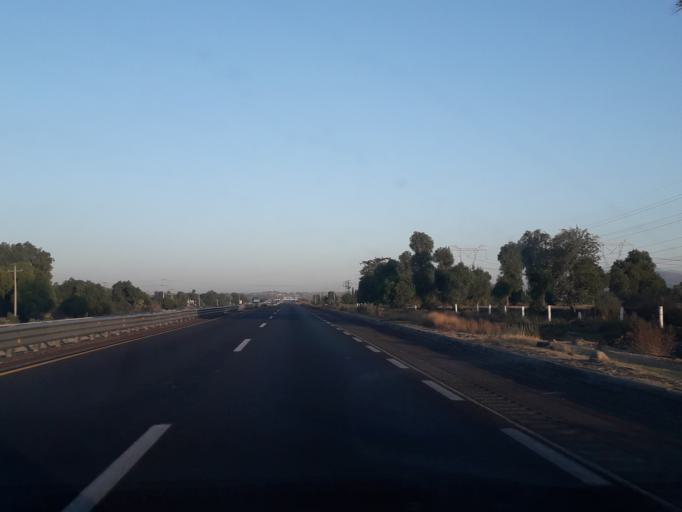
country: MX
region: Puebla
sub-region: Acatzingo
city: Progreso de Juarez
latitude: 18.9568
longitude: -97.7514
